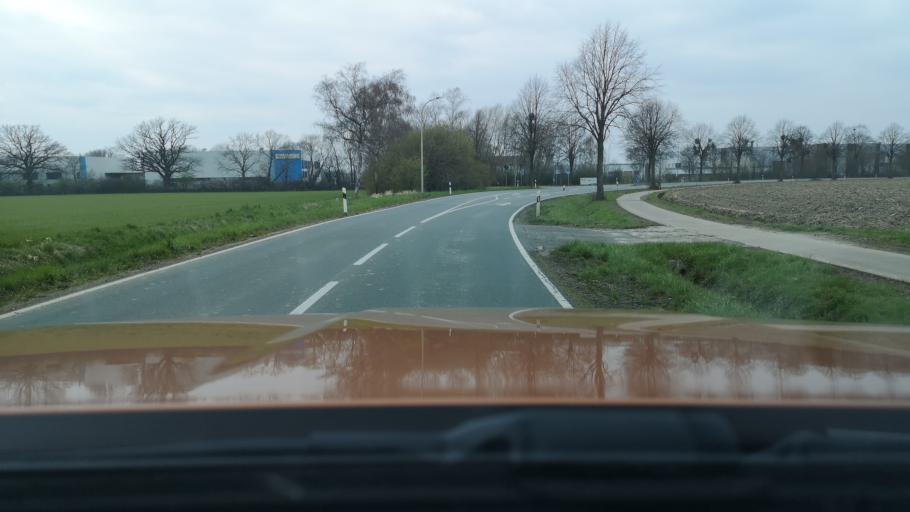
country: DE
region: Lower Saxony
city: Seggebruch
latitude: 52.2861
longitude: 9.1105
